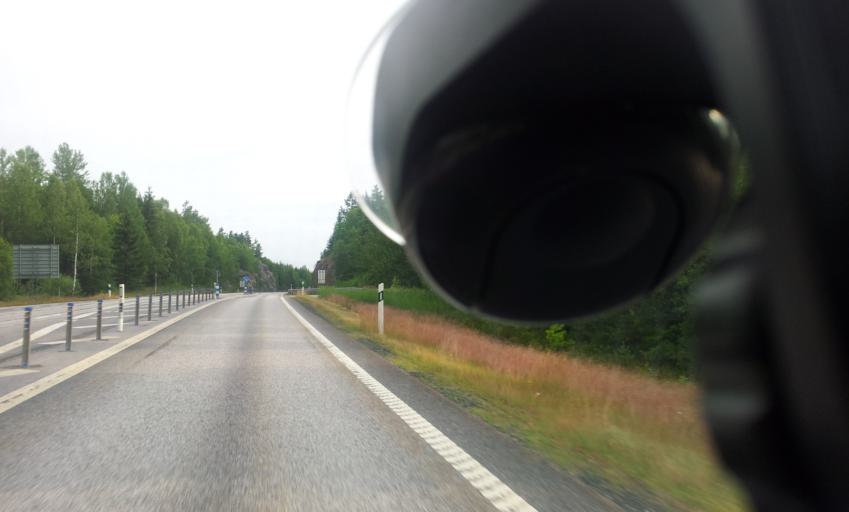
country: SE
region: OEstergoetland
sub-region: Valdemarsviks Kommun
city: Valdemarsvik
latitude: 58.1672
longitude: 16.5399
